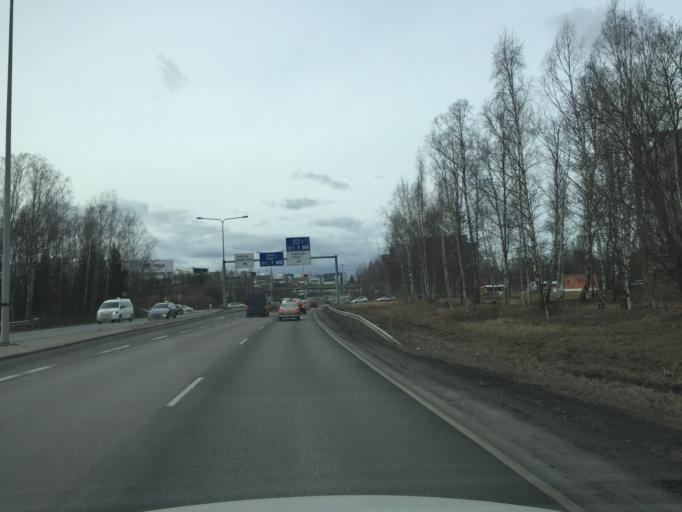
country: FI
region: Uusimaa
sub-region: Helsinki
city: Otaniemi
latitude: 60.1847
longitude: 24.8116
